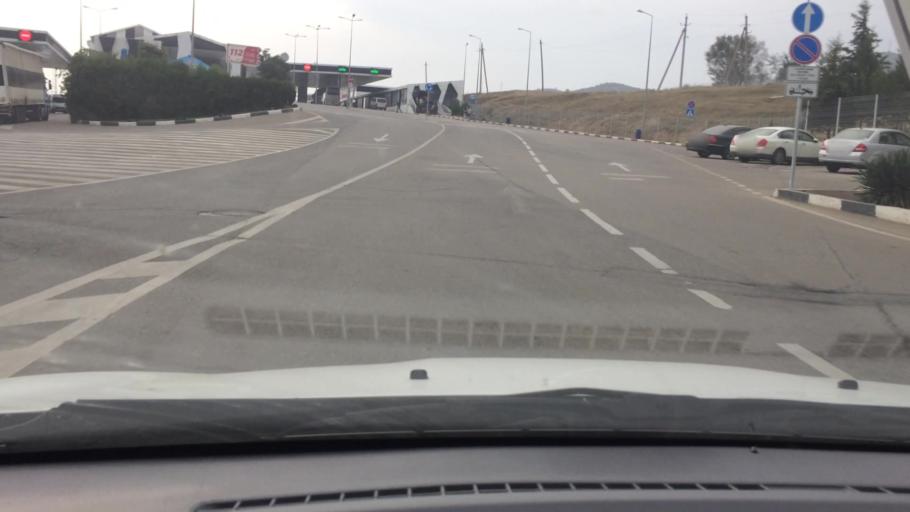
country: AM
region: Tavush
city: Bagratashen
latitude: 41.2282
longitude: 44.8289
